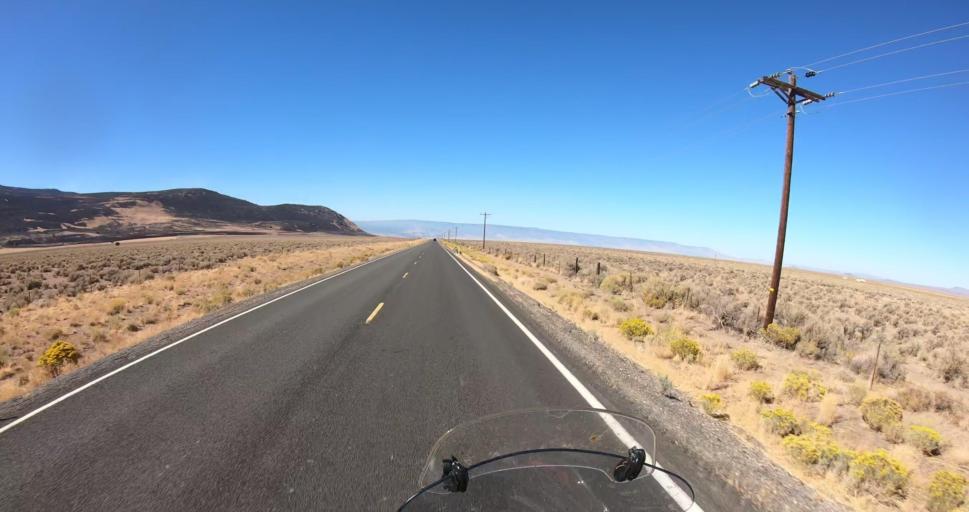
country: US
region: Oregon
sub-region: Lake County
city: Lakeview
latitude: 42.7087
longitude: -120.5586
